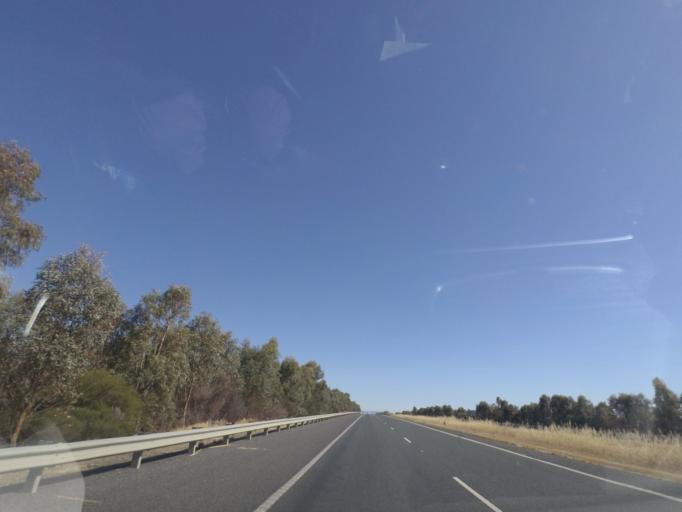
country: AU
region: Victoria
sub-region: Greater Shepparton
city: Shepparton
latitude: -36.7711
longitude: 145.1786
